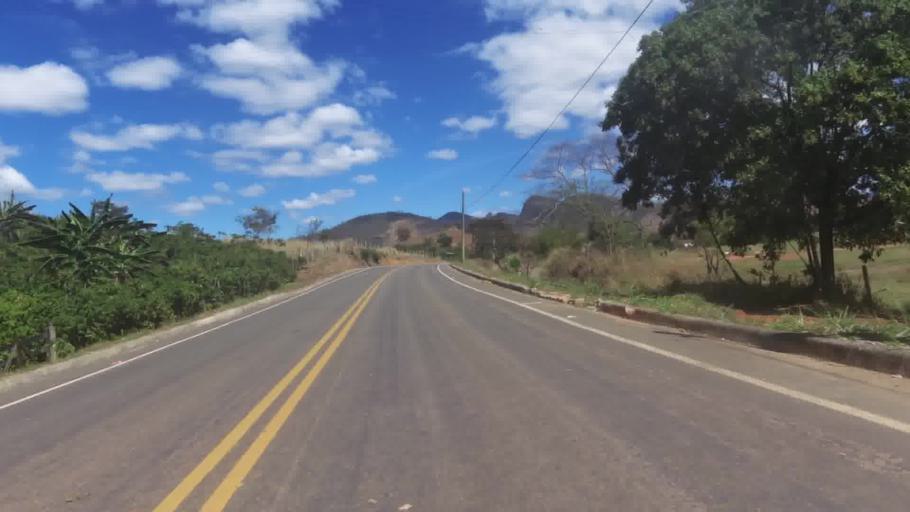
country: BR
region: Espirito Santo
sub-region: Cachoeiro De Itapemirim
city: Cachoeiro de Itapemirim
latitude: -20.9129
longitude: -41.2147
